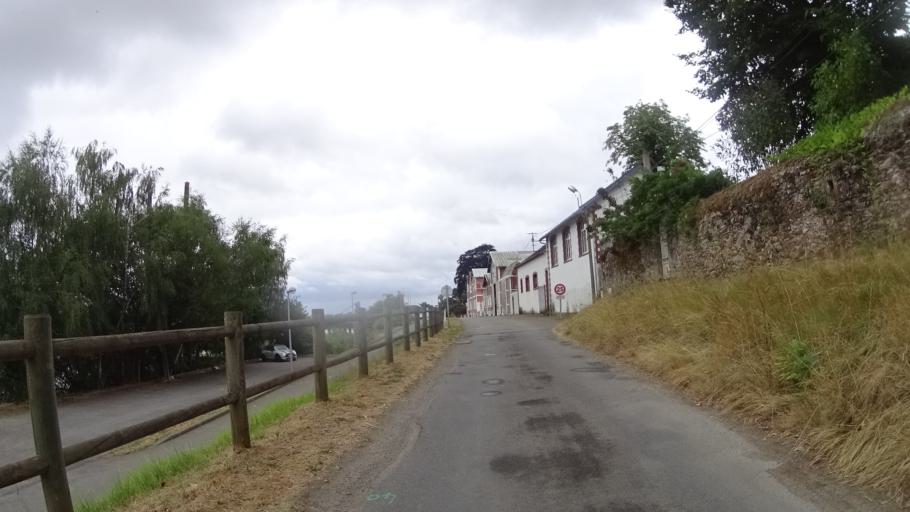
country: FR
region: Pays de la Loire
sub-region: Departement de la Loire-Atlantique
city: Le Pellerin
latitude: 47.2043
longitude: -1.7623
